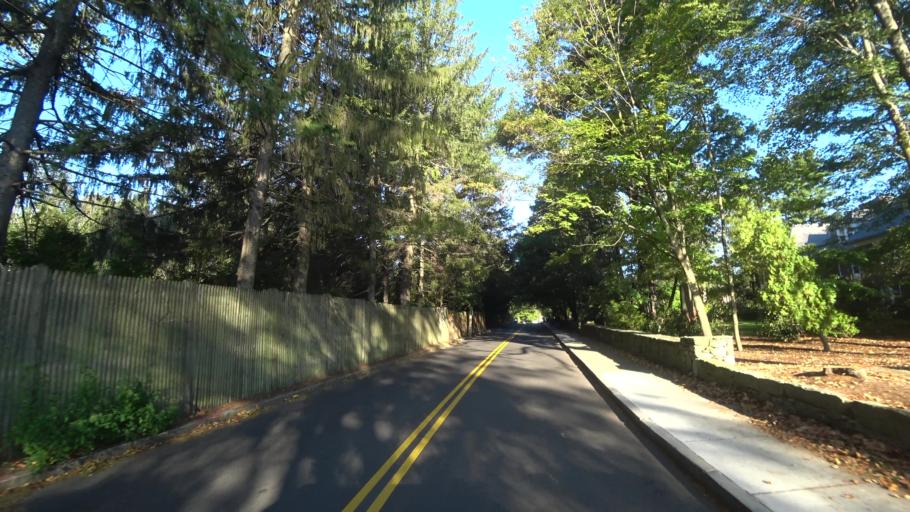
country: US
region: Massachusetts
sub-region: Middlesex County
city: Newton
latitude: 42.3315
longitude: -71.1712
